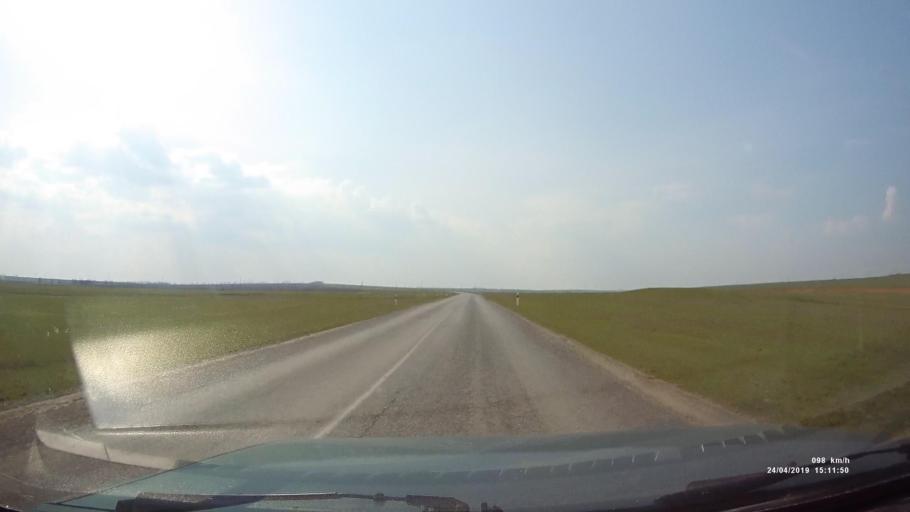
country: RU
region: Rostov
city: Remontnoye
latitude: 46.5449
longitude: 43.3135
